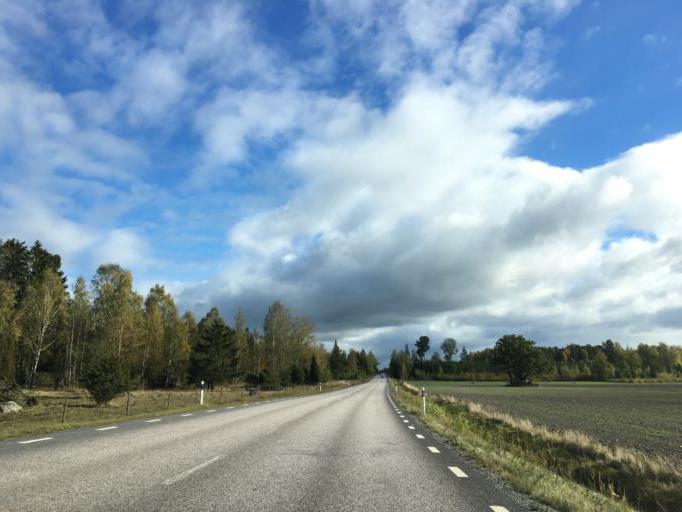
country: SE
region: Soedermanland
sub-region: Nykopings Kommun
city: Olstorp
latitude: 58.9077
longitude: 16.5668
